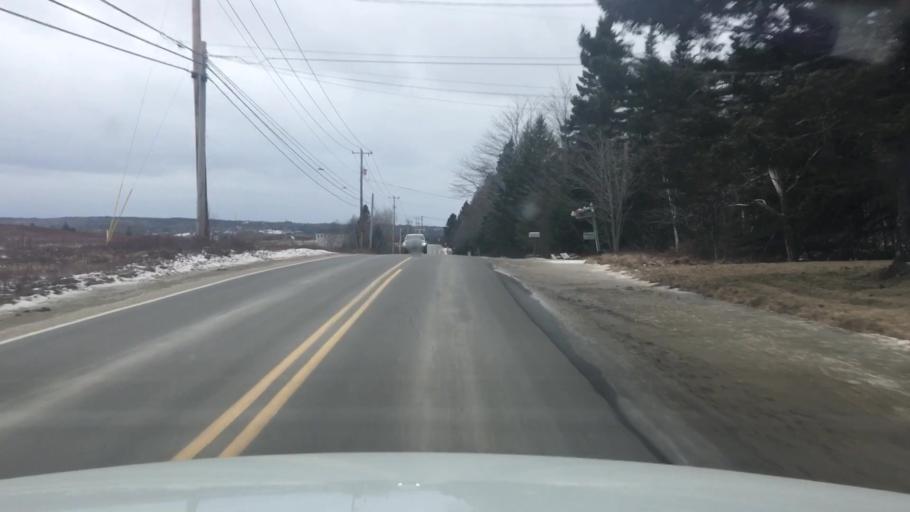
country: US
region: Maine
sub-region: Washington County
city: Addison
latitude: 44.6210
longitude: -67.7059
